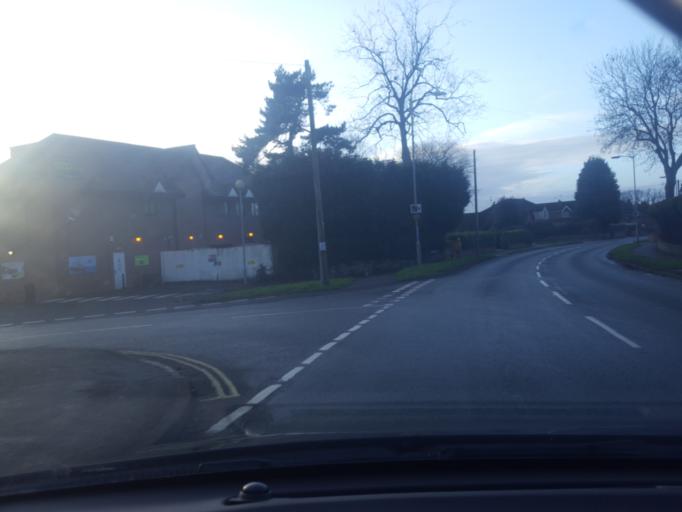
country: GB
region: England
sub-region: Staffordshire
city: Codsall
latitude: 52.6310
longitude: -2.2018
